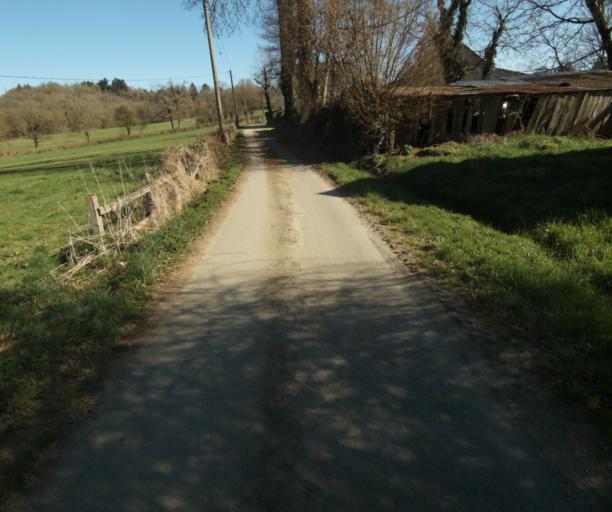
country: FR
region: Limousin
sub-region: Departement de la Correze
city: Chamboulive
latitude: 45.4324
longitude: 1.6490
